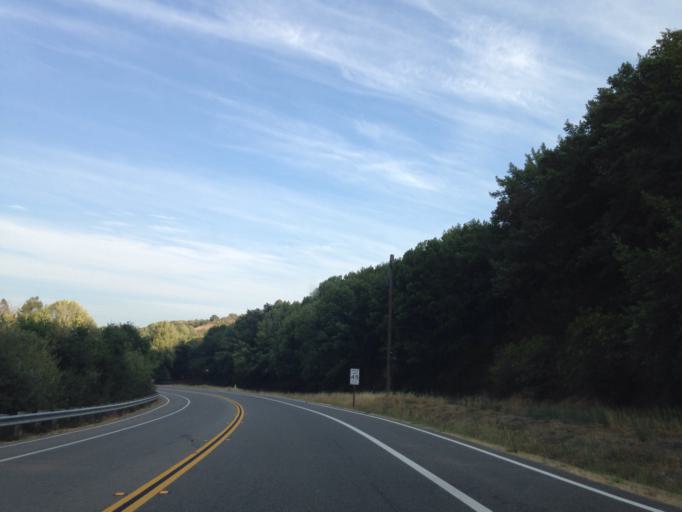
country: US
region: California
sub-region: Marin County
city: Lucas Valley-Marinwood
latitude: 38.0311
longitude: -122.5830
